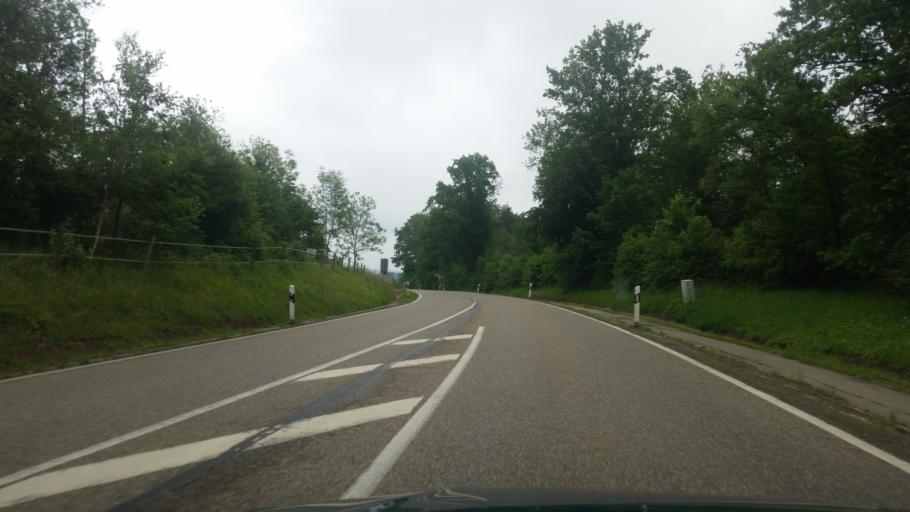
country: DE
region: Baden-Wuerttemberg
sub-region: Regierungsbezirk Stuttgart
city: Ellwangen
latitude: 48.9738
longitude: 10.1015
